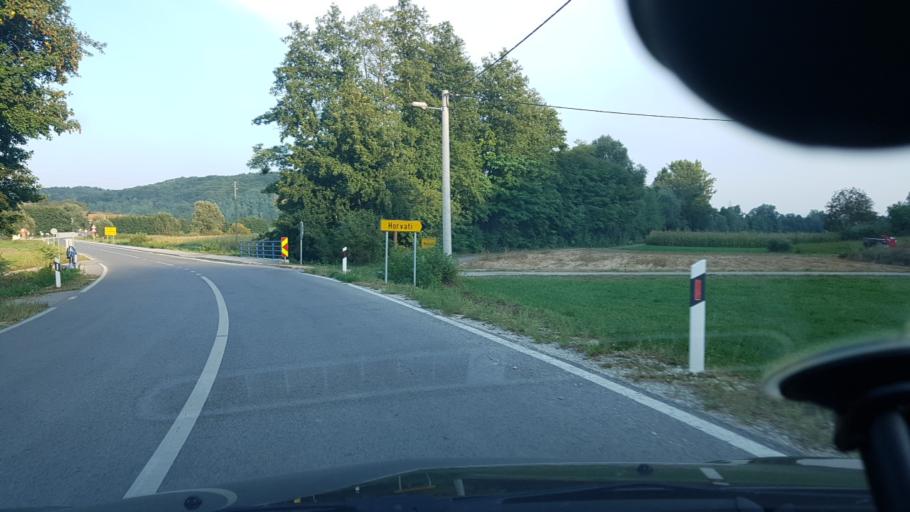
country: HR
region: Krapinsko-Zagorska
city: Pregrada
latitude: 46.1561
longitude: 15.7981
